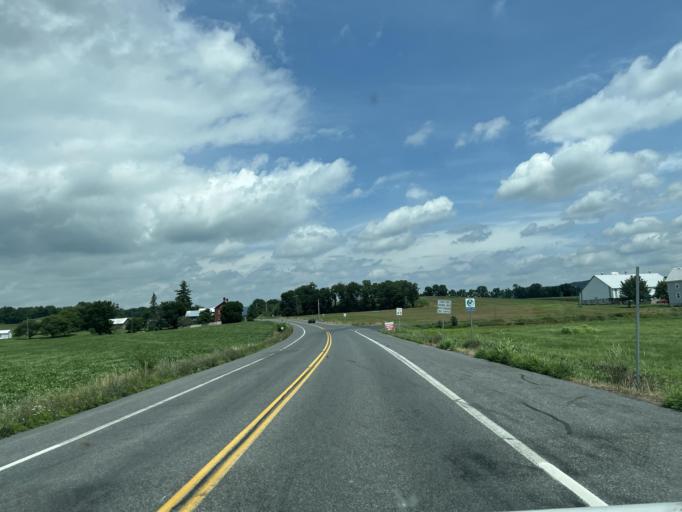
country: US
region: Pennsylvania
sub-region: Franklin County
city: Wayne Heights
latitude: 39.7201
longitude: -77.5435
